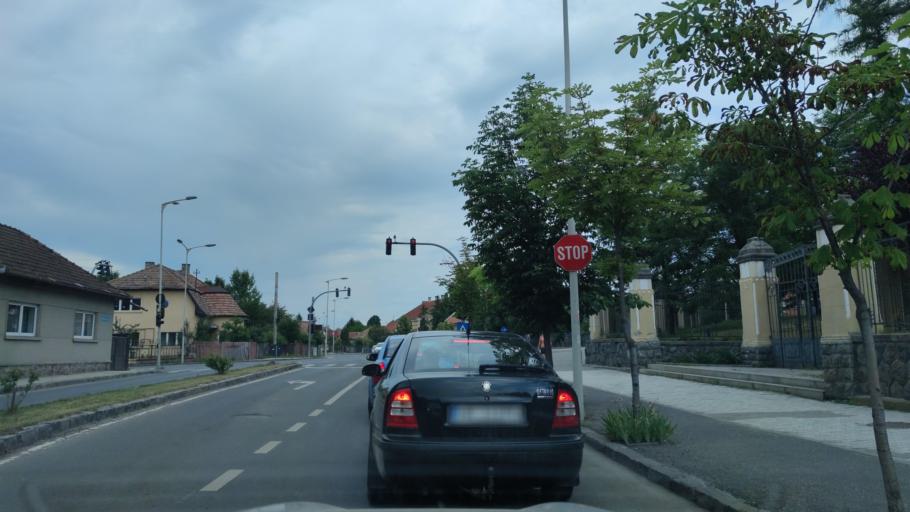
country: RO
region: Harghita
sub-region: Municipiul Miercurea Ciuc
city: Miercurea-Ciuc
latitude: 46.3679
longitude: 25.8059
